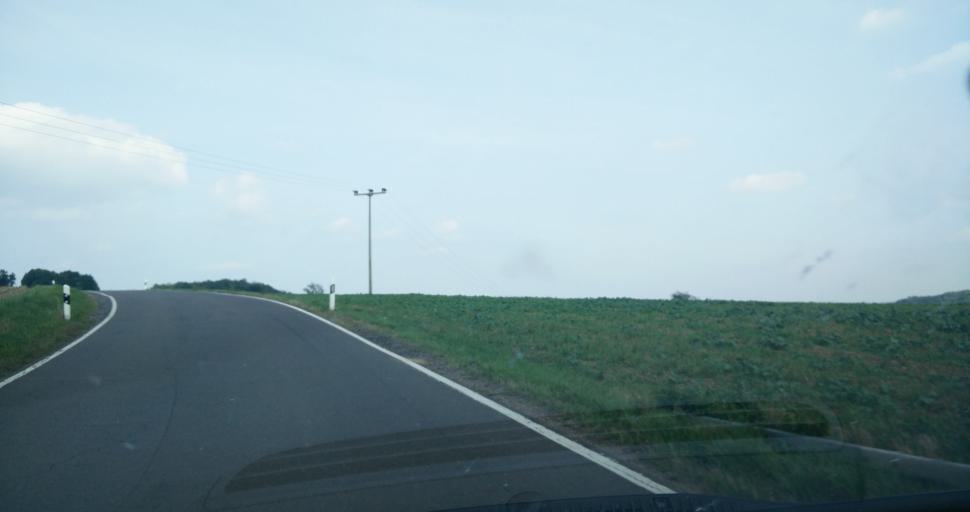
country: DE
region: Saxony
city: Rochlitz
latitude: 51.0786
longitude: 12.7905
